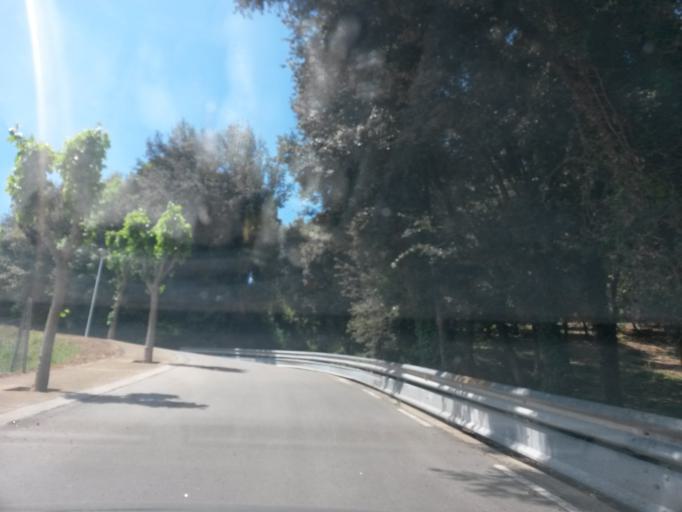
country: ES
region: Catalonia
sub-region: Provincia de Girona
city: Vilablareix
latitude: 41.9634
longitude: 2.7614
